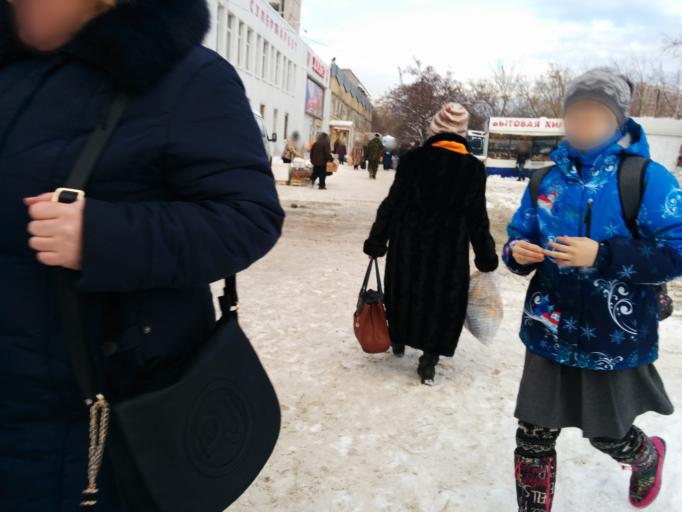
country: RU
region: Perm
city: Perm
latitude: 57.9814
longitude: 56.2922
